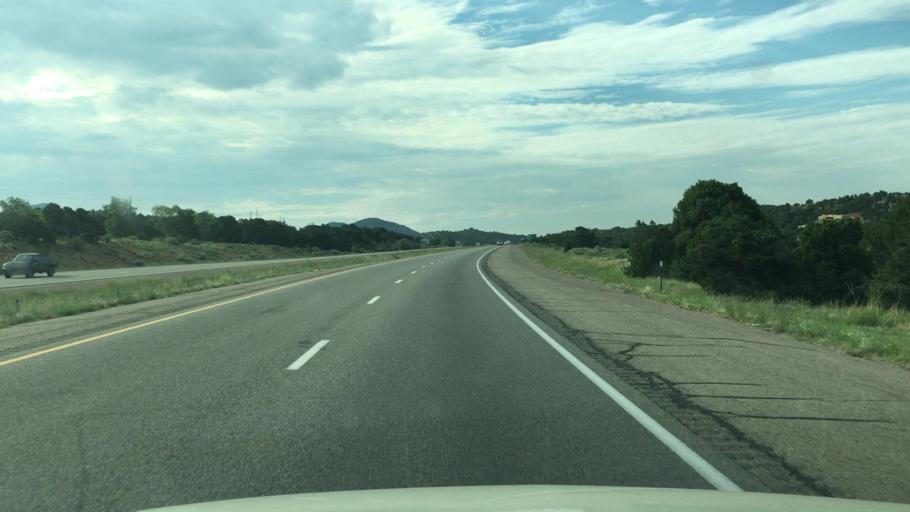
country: US
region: New Mexico
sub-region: Santa Fe County
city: Santa Fe
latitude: 35.6326
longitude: -105.9258
